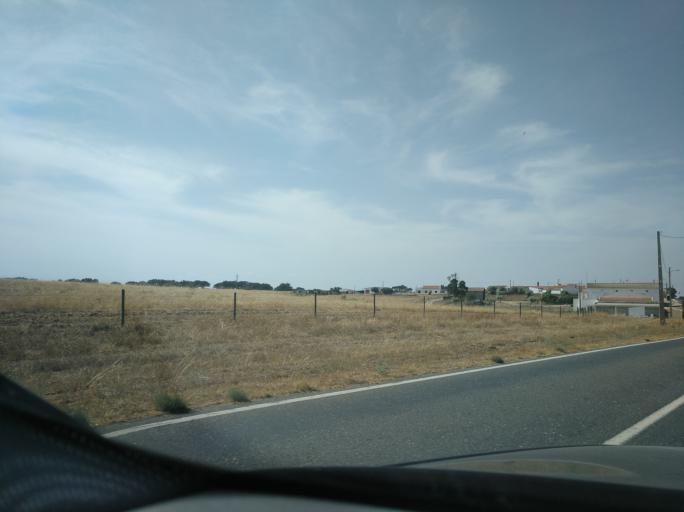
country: PT
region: Beja
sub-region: Mertola
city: Mertola
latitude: 37.7594
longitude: -7.8127
